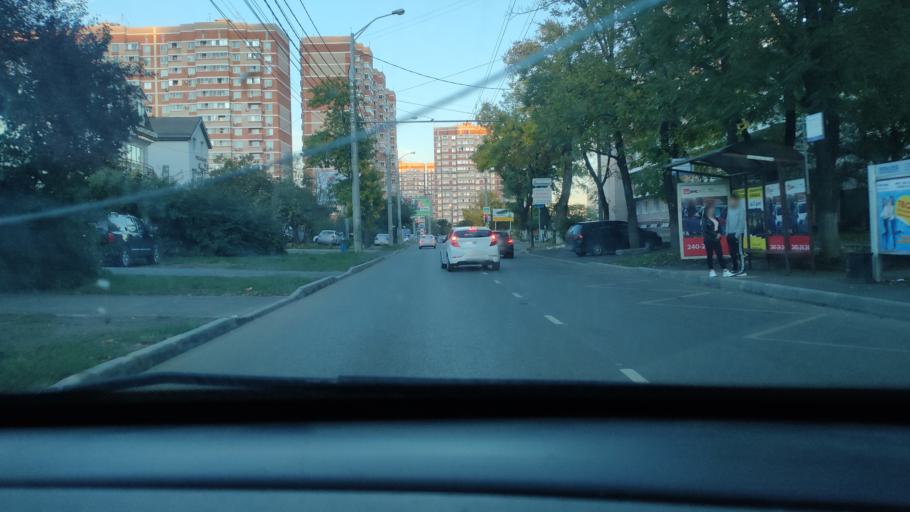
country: RU
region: Krasnodarskiy
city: Krasnodar
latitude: 45.0386
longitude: 38.9467
